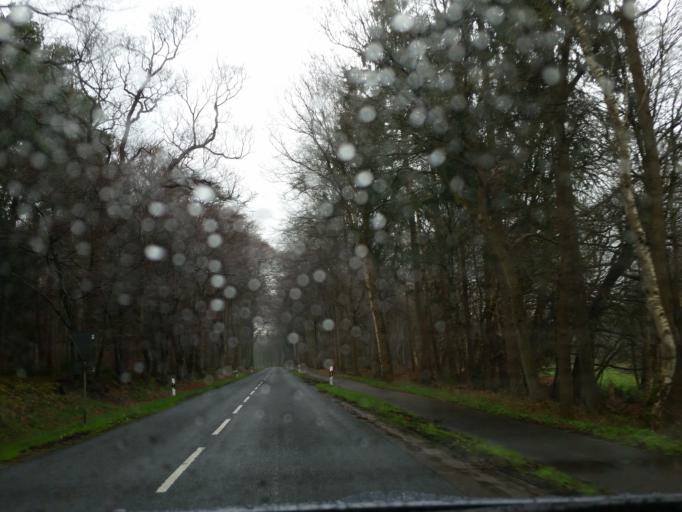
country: DE
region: Lower Saxony
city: Hipstedt
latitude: 53.5033
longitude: 8.9787
